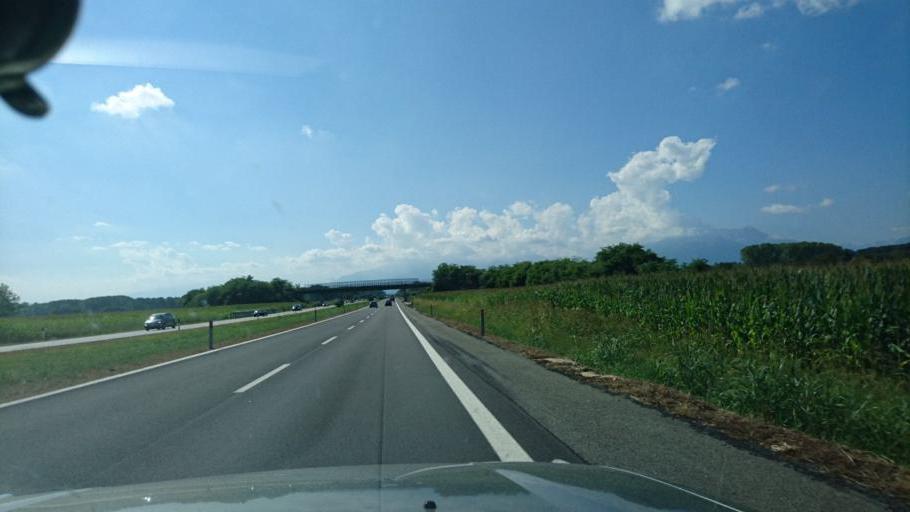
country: IT
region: Piedmont
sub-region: Provincia di Torino
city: Azeglio
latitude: 45.4156
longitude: 7.9899
